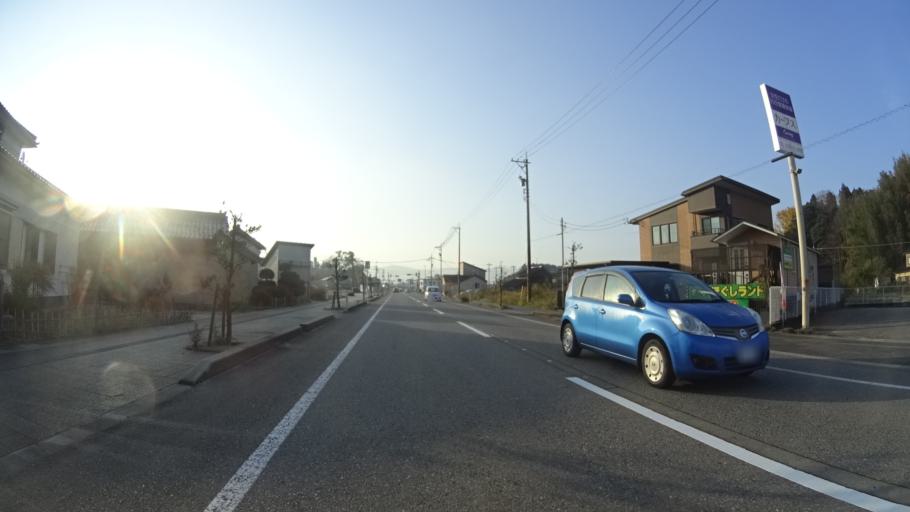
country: JP
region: Ishikawa
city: Nanao
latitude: 37.0498
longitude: 136.9567
